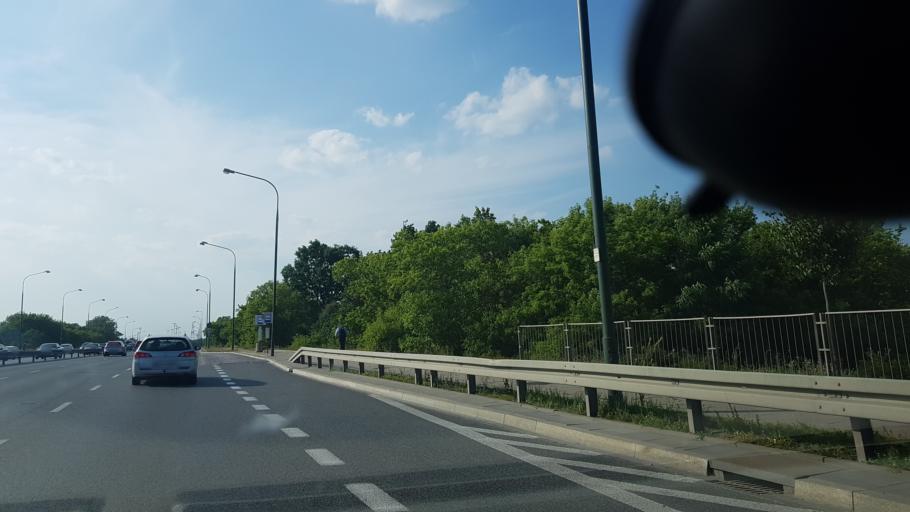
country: PL
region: Masovian Voivodeship
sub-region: Warszawa
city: Zoliborz
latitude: 52.2990
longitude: 20.9943
